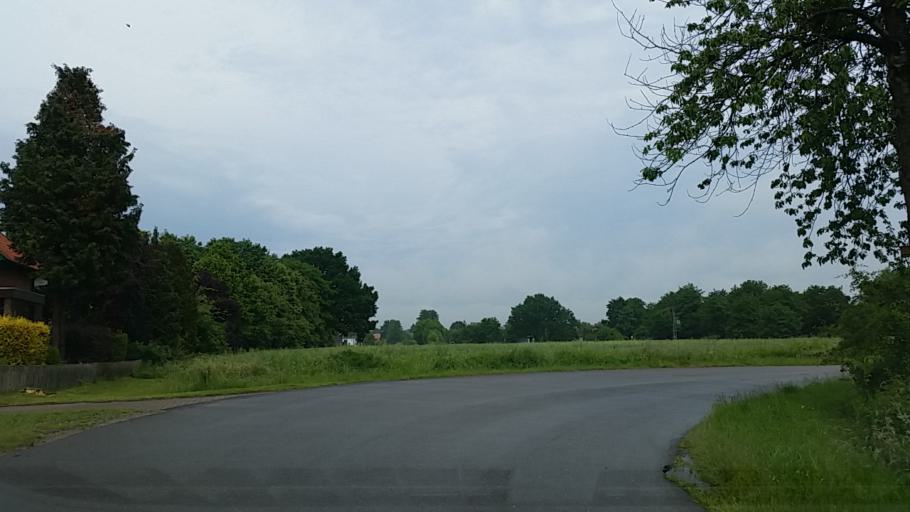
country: DE
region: Schleswig-Holstein
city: Escheburg
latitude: 53.4212
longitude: 10.3152
